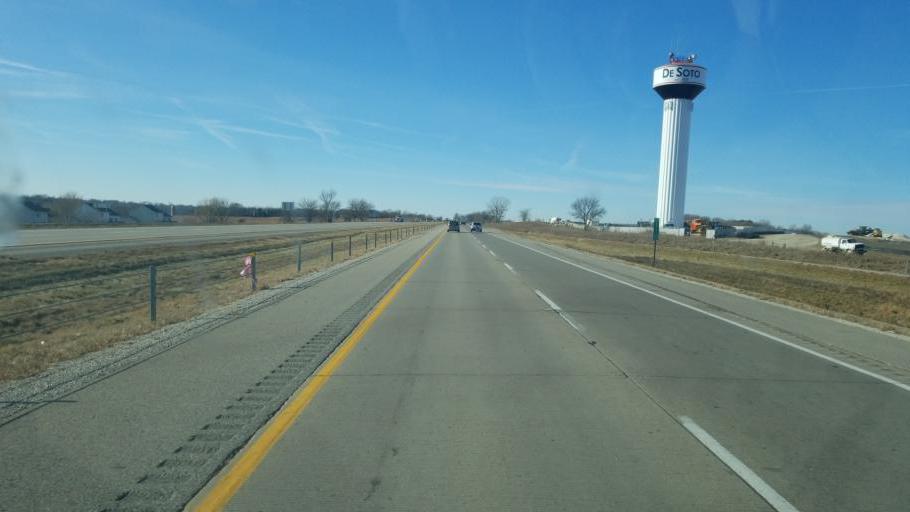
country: US
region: Iowa
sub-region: Dallas County
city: De Soto
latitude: 41.5401
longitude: -94.0147
